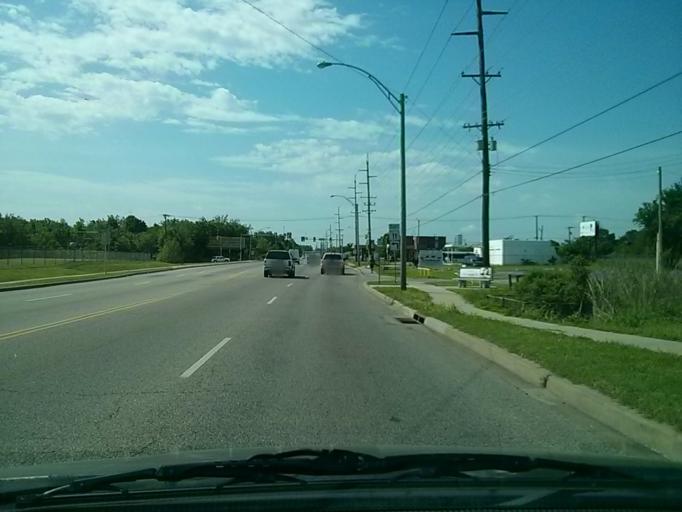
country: US
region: Oklahoma
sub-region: Tulsa County
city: Turley
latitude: 36.2075
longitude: -95.9757
